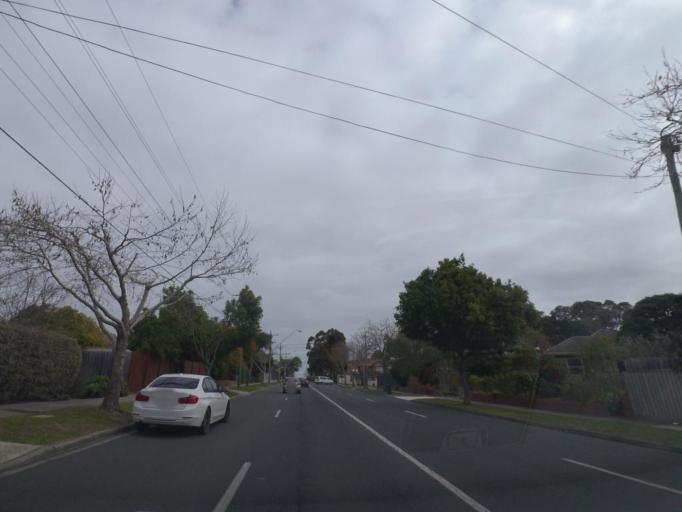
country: AU
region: Victoria
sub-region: Whitehorse
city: Mont Albert North
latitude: -37.8009
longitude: 145.1120
